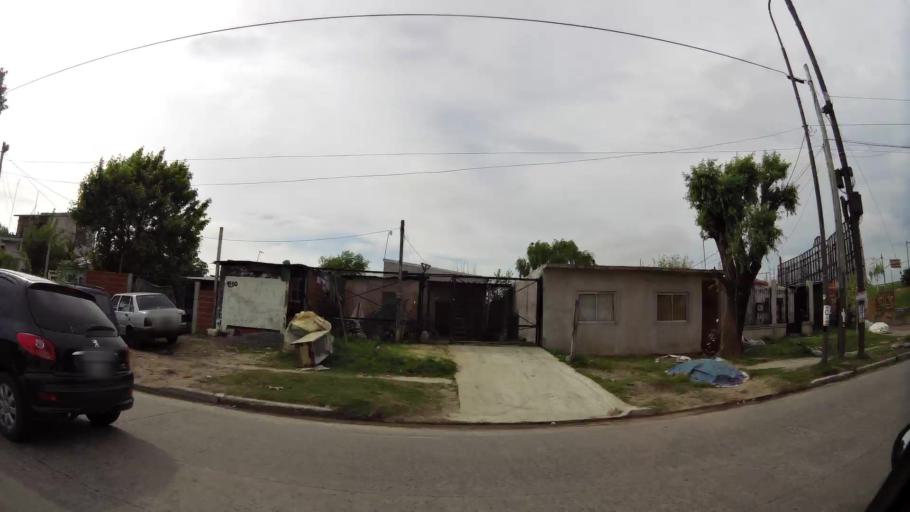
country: AR
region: Buenos Aires
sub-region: Partido de Quilmes
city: Quilmes
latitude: -34.7164
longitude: -58.2335
